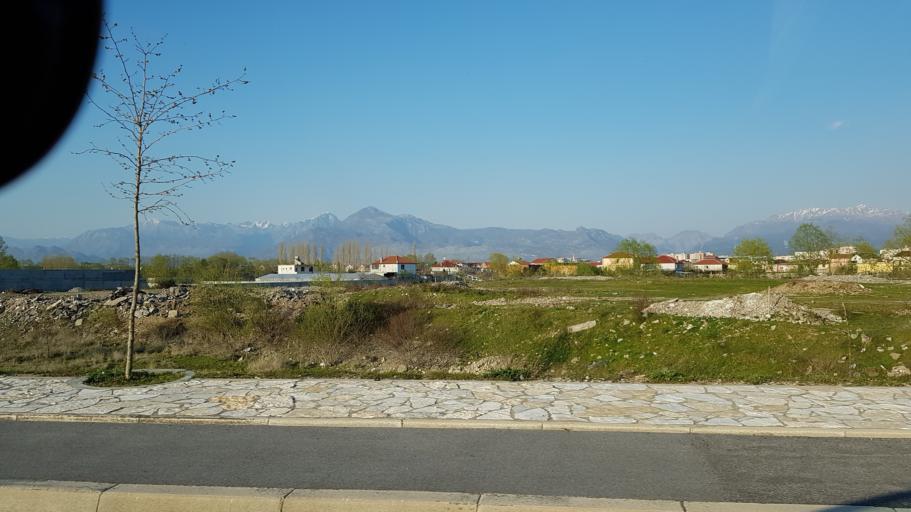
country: AL
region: Shkoder
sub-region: Rrethi i Shkodres
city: Shkoder
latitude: 42.0641
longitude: 19.4917
